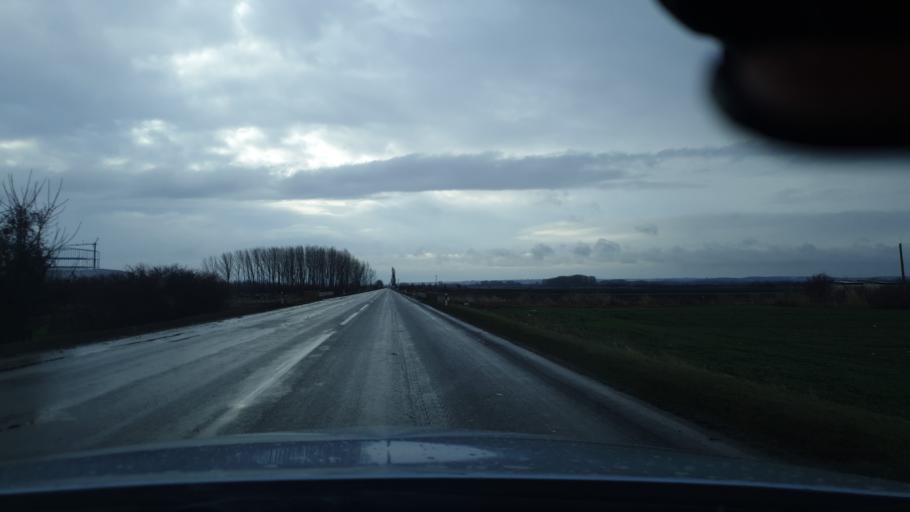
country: RS
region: Autonomna Pokrajina Vojvodina
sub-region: Juznobanatski Okrug
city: Kovin
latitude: 44.7302
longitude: 20.9650
